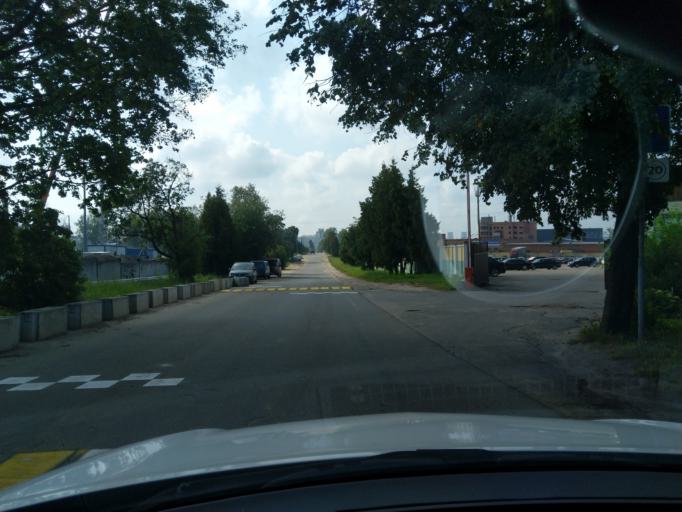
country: BY
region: Minsk
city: Zhdanovichy
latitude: 53.9056
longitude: 27.4139
